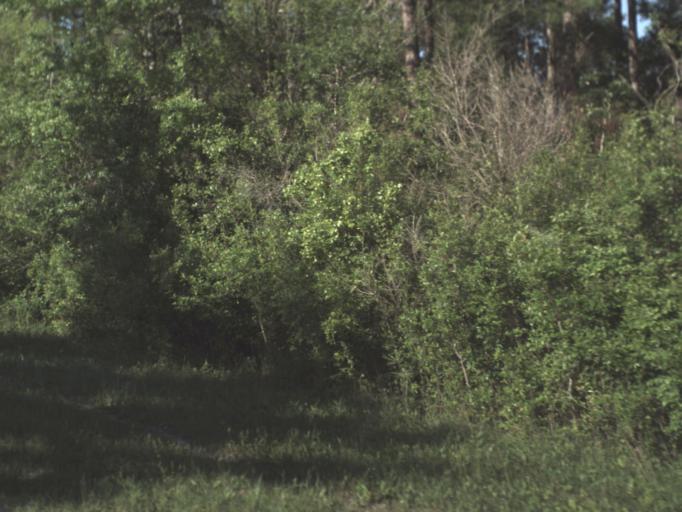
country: US
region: Florida
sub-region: Gulf County
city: Wewahitchka
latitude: 30.0308
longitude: -84.9836
